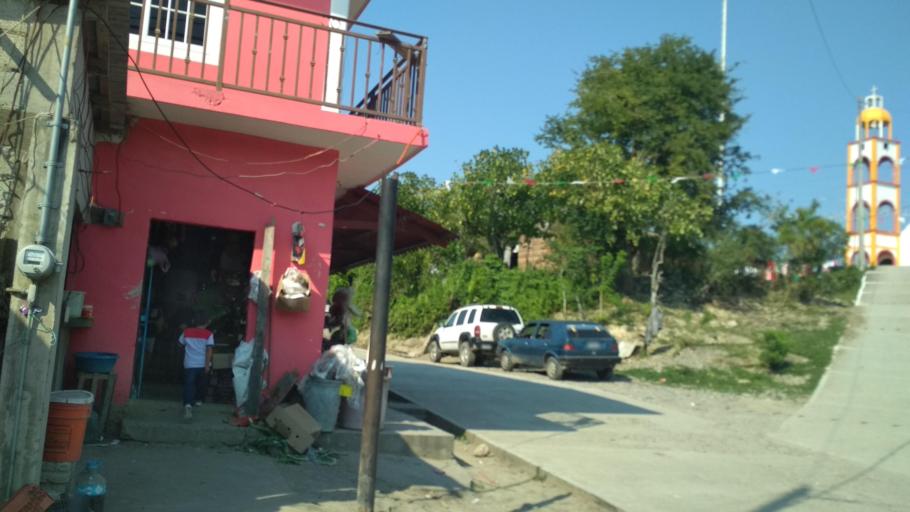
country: MX
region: Veracruz
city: Agua Dulce
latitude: 20.3873
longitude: -97.2134
